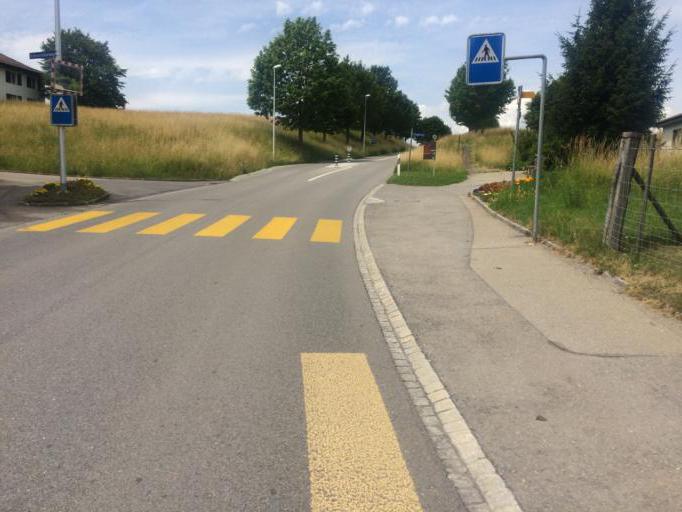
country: CH
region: Bern
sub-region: Seeland District
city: Seedorf
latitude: 47.0276
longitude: 7.3304
